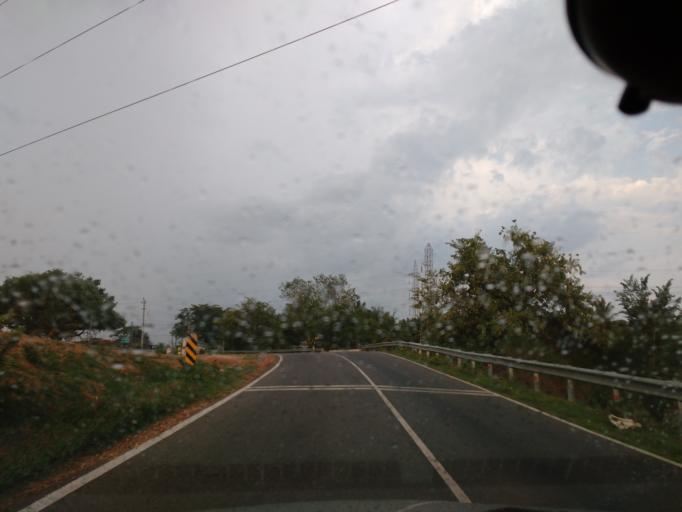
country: IN
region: Karnataka
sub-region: Tumkur
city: Tiptur
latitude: 13.2830
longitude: 76.5608
